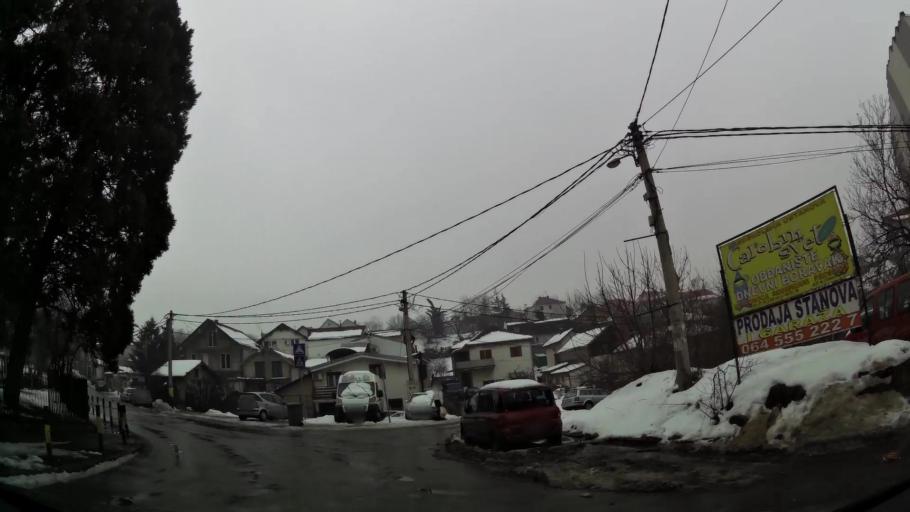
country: RS
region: Central Serbia
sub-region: Belgrade
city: Zvezdara
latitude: 44.7822
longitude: 20.5159
